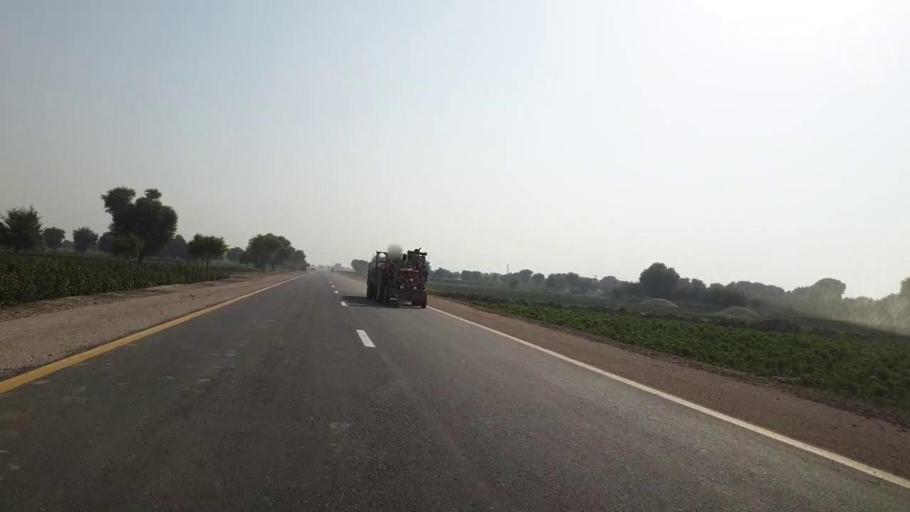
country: PK
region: Sindh
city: Bhan
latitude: 26.5221
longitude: 67.7883
